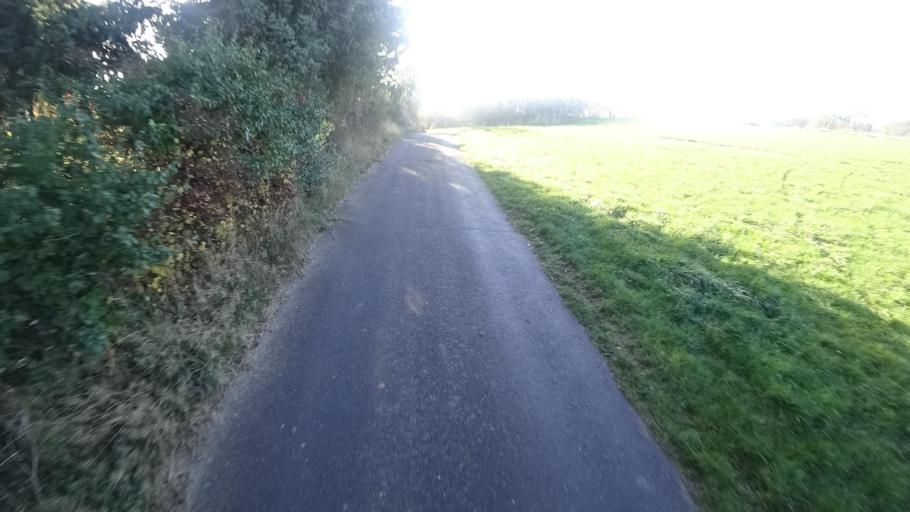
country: DE
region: Rheinland-Pfalz
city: Berg
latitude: 50.5279
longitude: 6.9426
